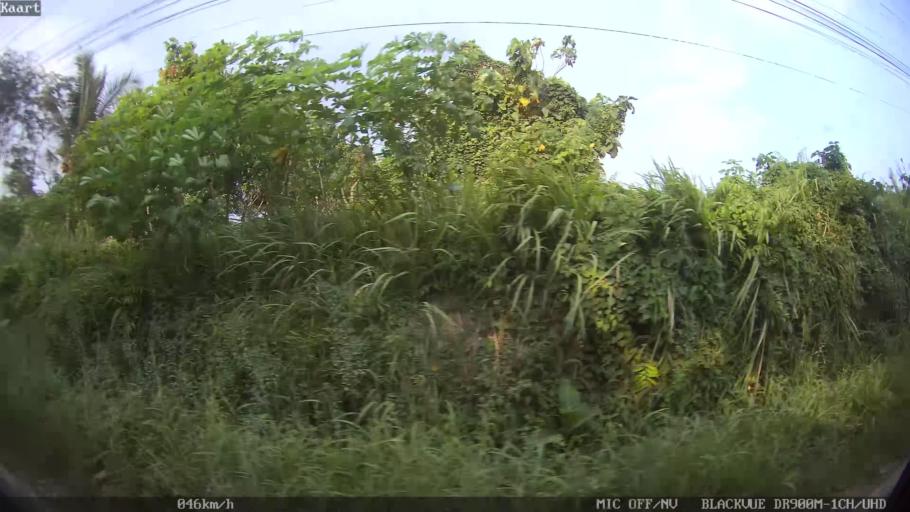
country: ID
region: Lampung
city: Kedaton
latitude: -5.3790
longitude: 105.1968
